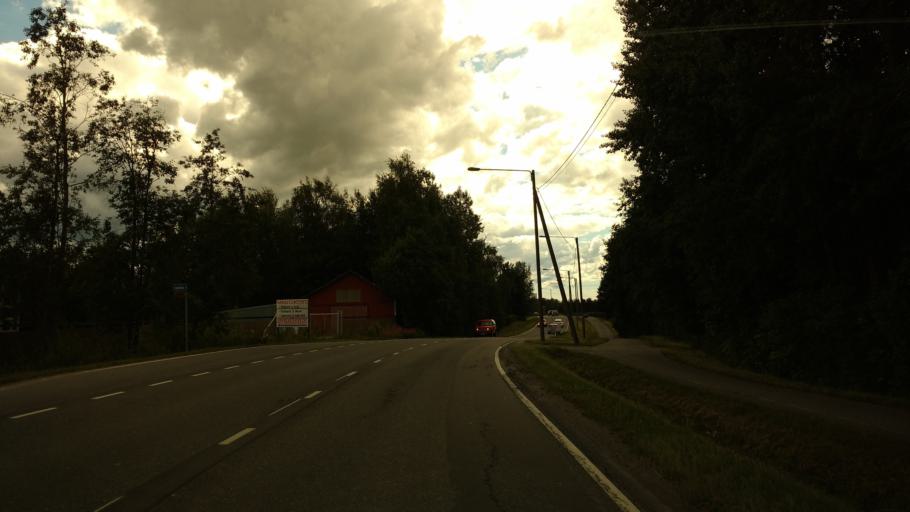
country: FI
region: Varsinais-Suomi
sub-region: Salo
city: Salo
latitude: 60.4023
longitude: 23.1649
